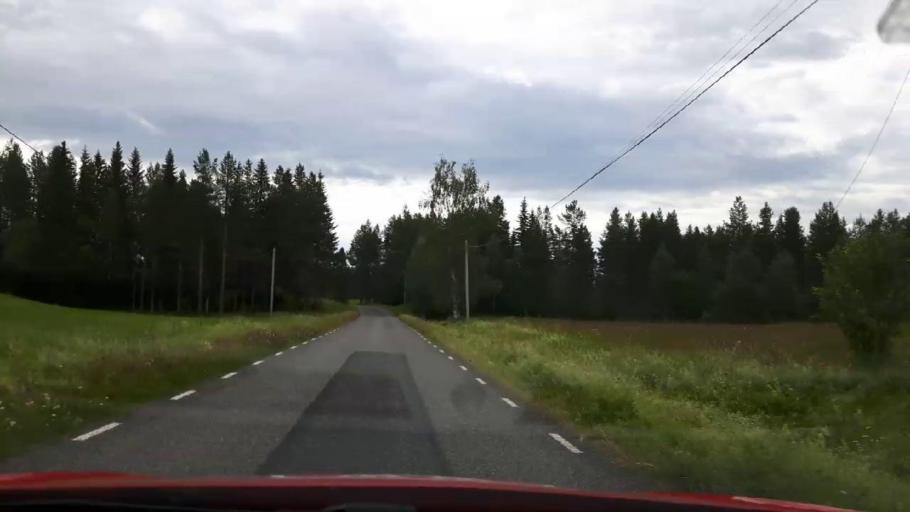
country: SE
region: Jaemtland
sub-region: OEstersunds Kommun
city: Lit
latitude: 63.3860
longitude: 15.0295
